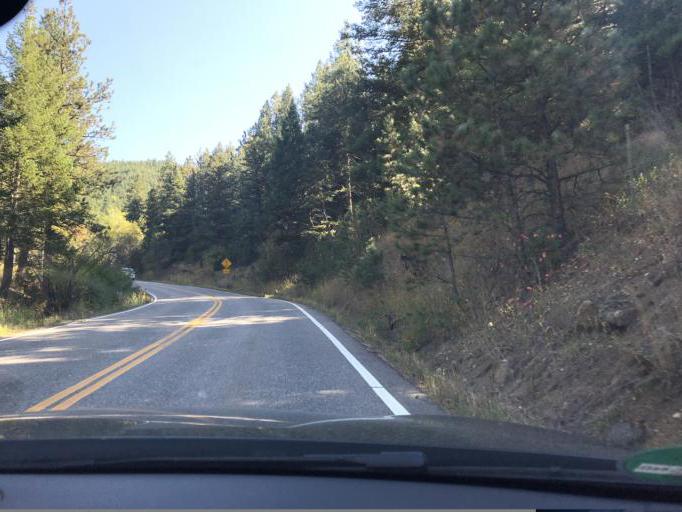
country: US
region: Colorado
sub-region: Boulder County
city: Boulder
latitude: 40.0911
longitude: -105.3515
